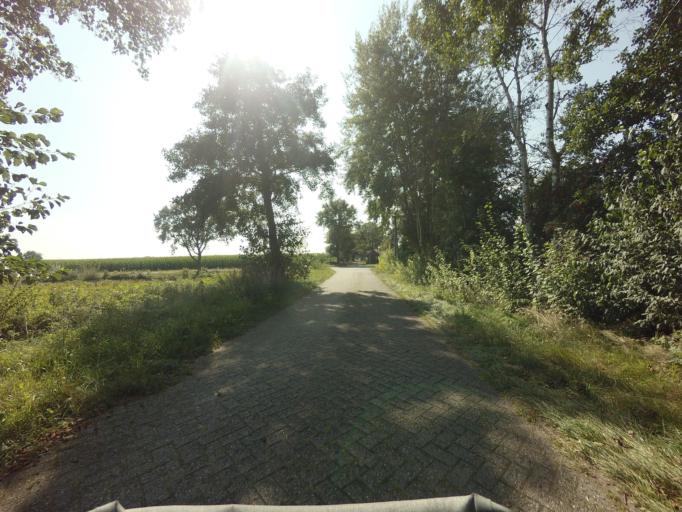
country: DE
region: Lower Saxony
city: Emlichheim
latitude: 52.5798
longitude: 6.8345
